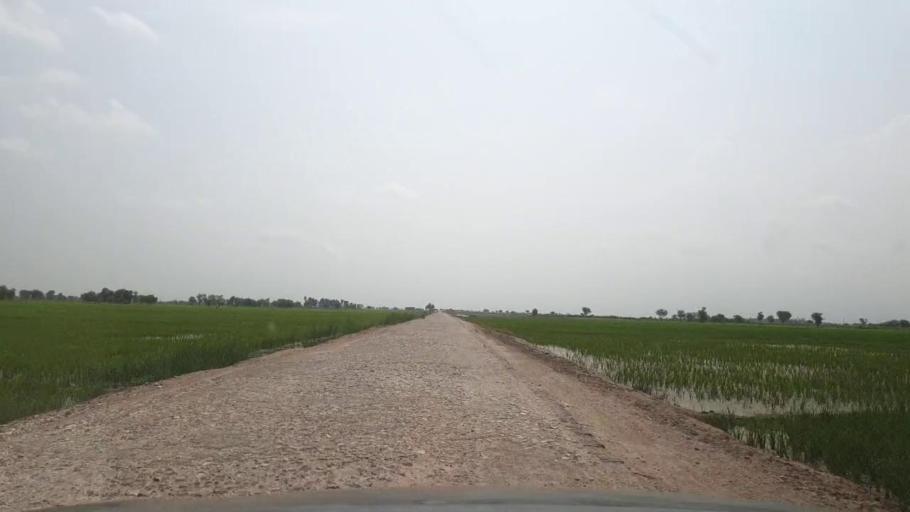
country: PK
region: Sindh
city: Ratodero
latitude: 27.8404
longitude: 68.3268
